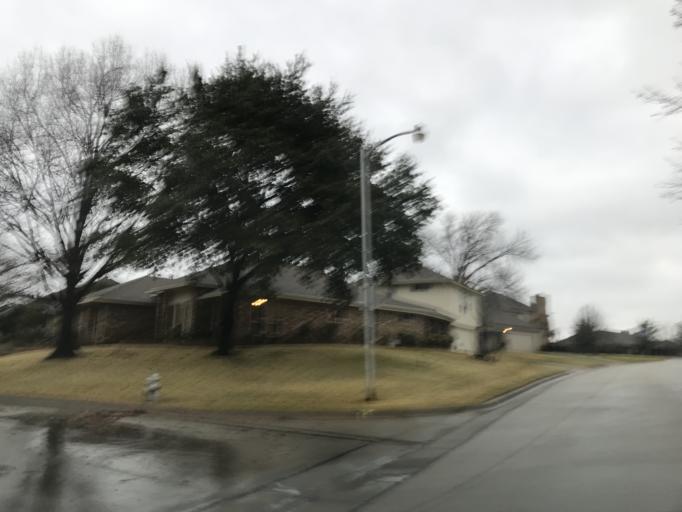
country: US
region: Texas
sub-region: Tarrant County
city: Arlington
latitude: 32.7741
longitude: -97.1029
